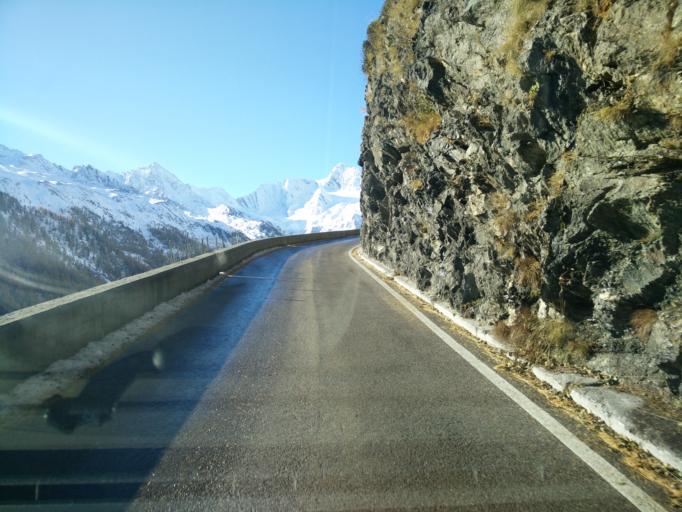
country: IT
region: Trentino-Alto Adige
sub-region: Bolzano
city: Moso in Passiria
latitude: 46.8841
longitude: 11.1181
